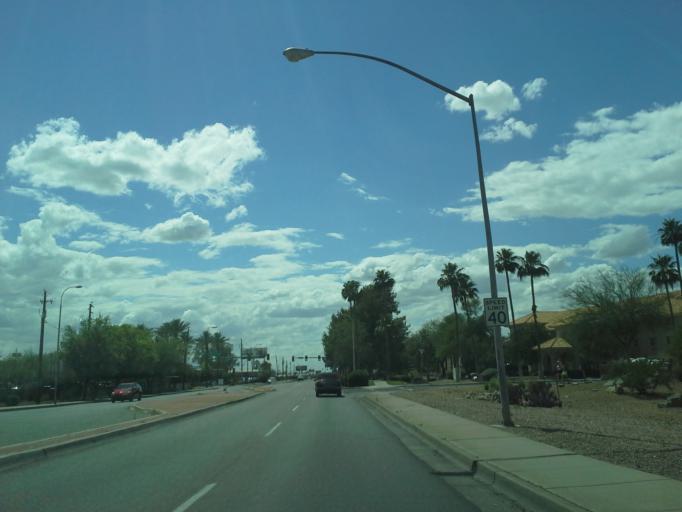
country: US
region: Arizona
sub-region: Maricopa County
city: Tempe Junction
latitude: 33.4220
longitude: -111.9794
